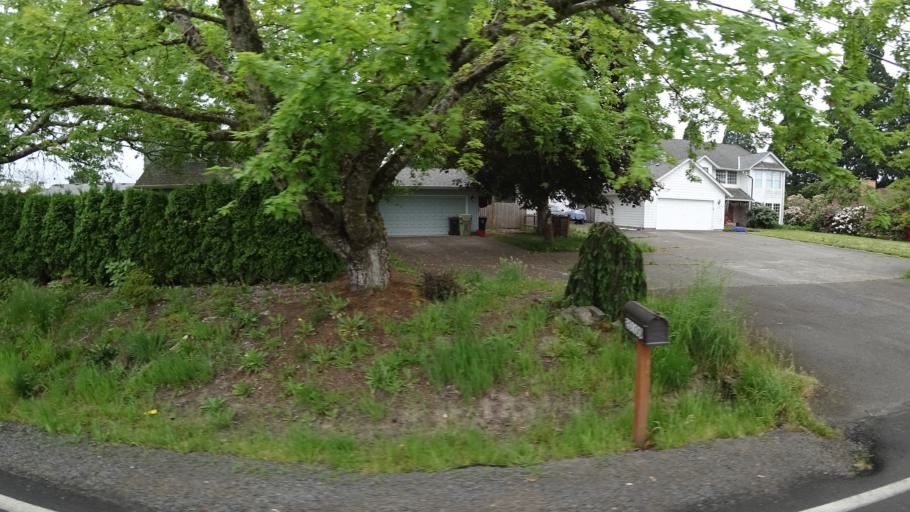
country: US
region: Oregon
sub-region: Washington County
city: Rockcreek
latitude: 45.5609
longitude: -122.8844
